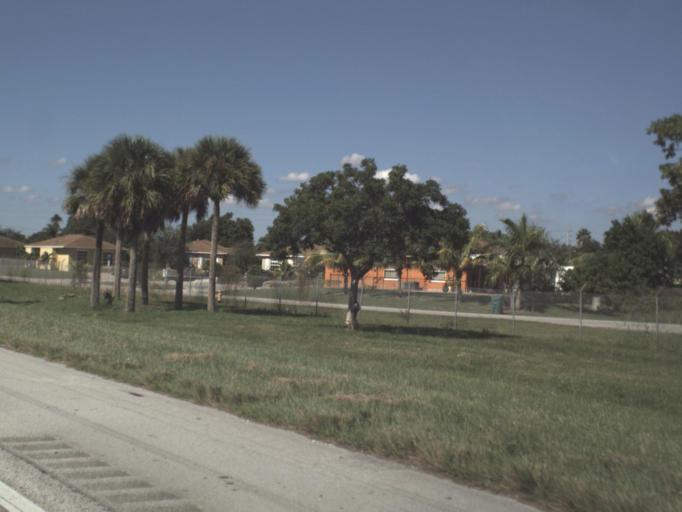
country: US
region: Florida
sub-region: Miami-Dade County
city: Princeton
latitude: 25.5287
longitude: -80.3929
